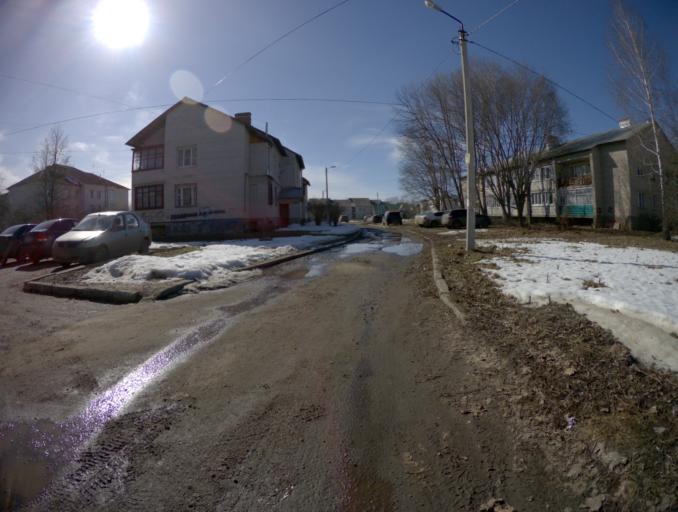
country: RU
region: Vladimir
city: Suzdal'
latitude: 56.4366
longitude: 40.4542
